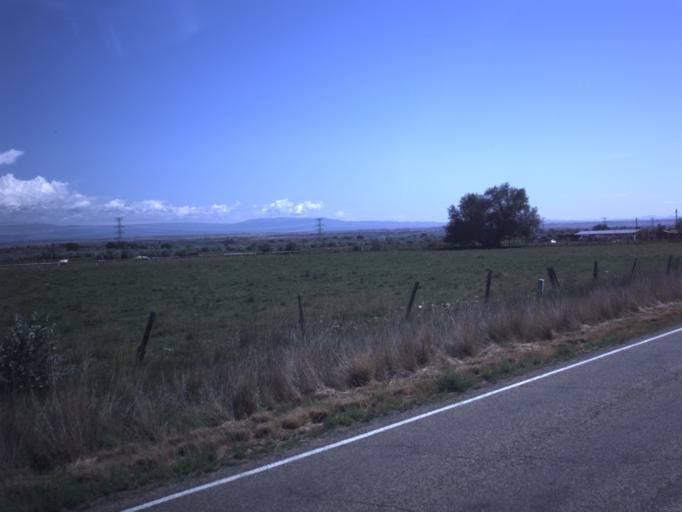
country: US
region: Utah
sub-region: Duchesne County
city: Roosevelt
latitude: 40.2584
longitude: -110.0978
